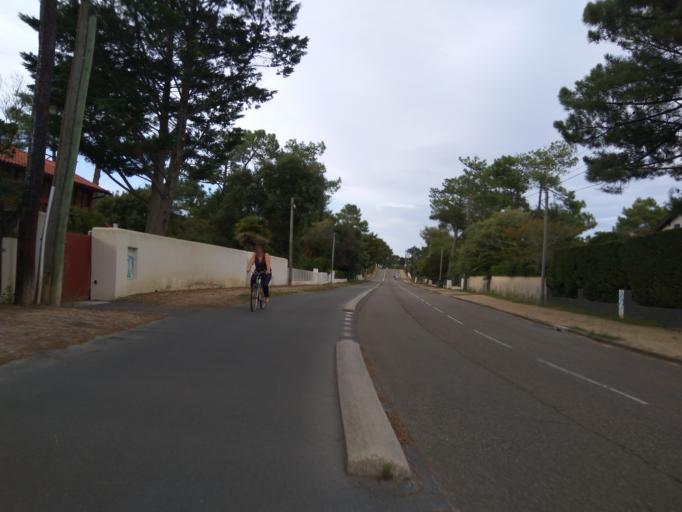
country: FR
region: Aquitaine
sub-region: Departement des Landes
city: Capbreton
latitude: 43.6418
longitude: -1.4417
